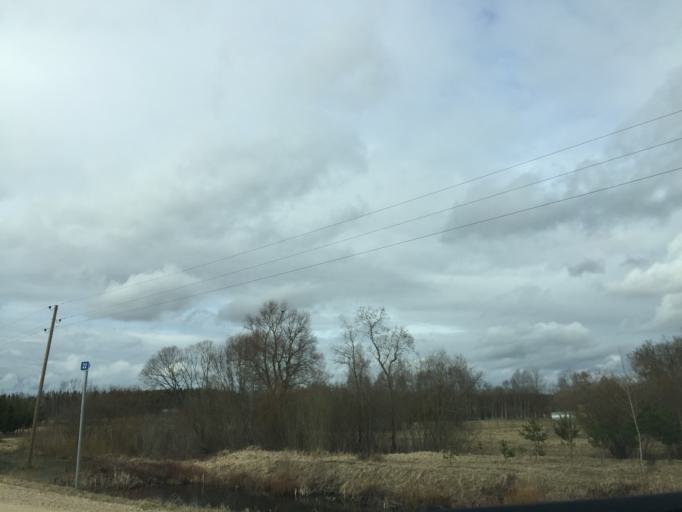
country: LV
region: Daugavpils
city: Daugavpils
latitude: 55.9518
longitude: 26.7010
